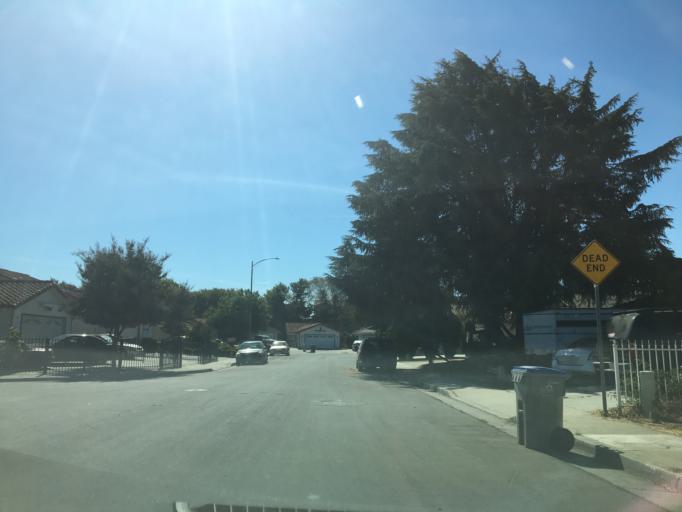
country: US
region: California
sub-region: Santa Clara County
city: Seven Trees
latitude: 37.3069
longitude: -121.8473
